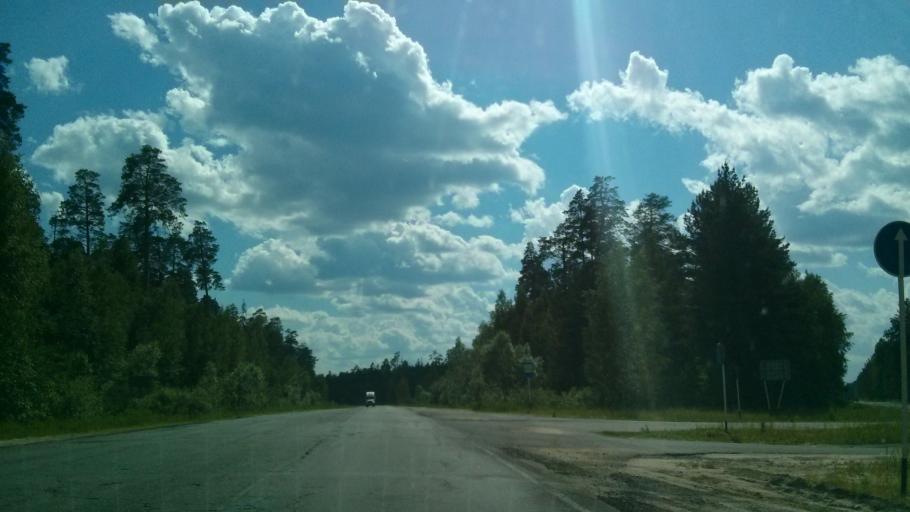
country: RU
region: Vladimir
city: Melenki
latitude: 55.3538
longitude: 41.6804
